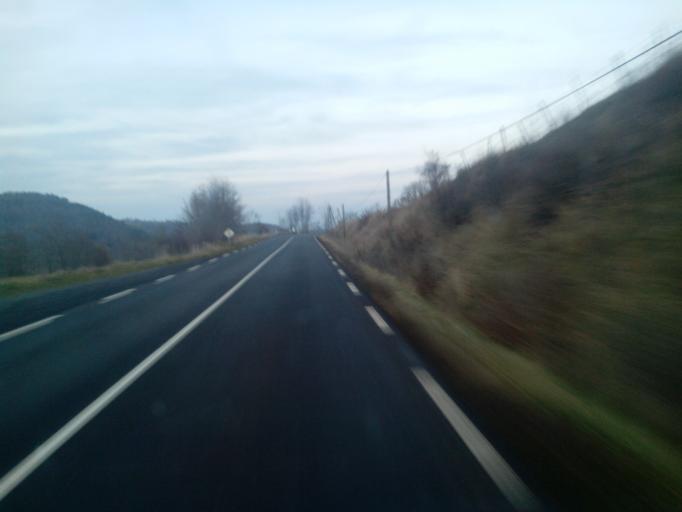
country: FR
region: Auvergne
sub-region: Departement du Cantal
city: Murat
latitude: 45.1004
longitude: 2.8862
